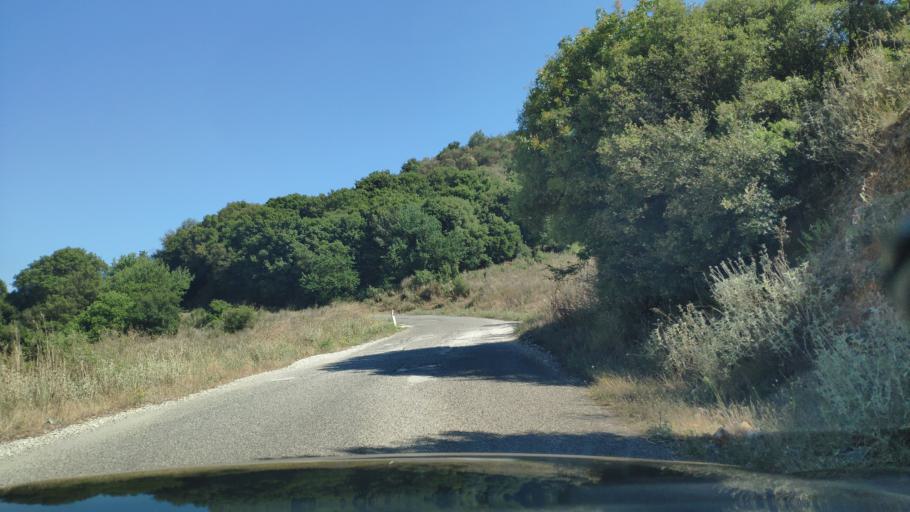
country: GR
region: West Greece
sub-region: Nomos Aitolias kai Akarnanias
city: Katouna
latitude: 38.8062
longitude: 21.1102
